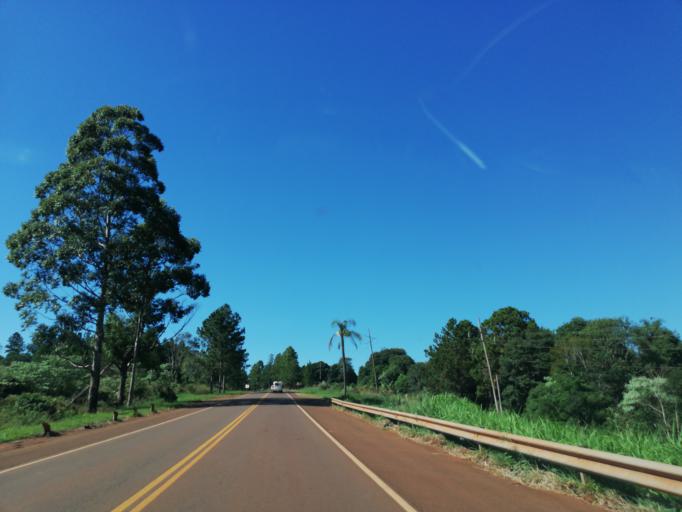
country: AR
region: Misiones
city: Dos de Mayo
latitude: -27.0476
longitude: -54.4358
